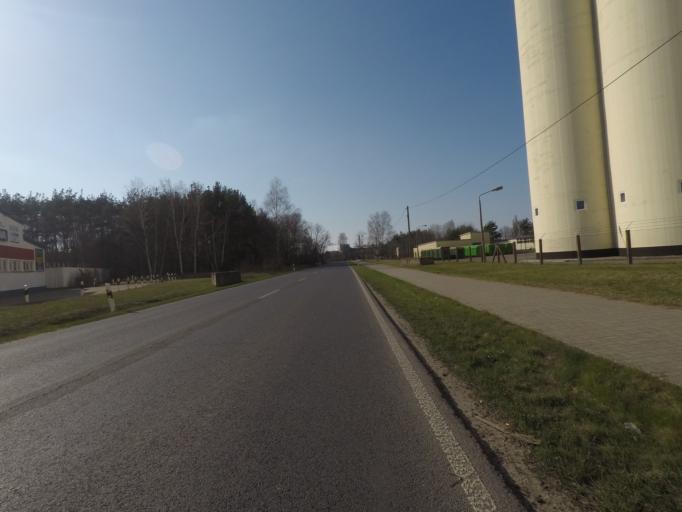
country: DE
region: Brandenburg
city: Eberswalde
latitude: 52.8482
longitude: 13.7866
